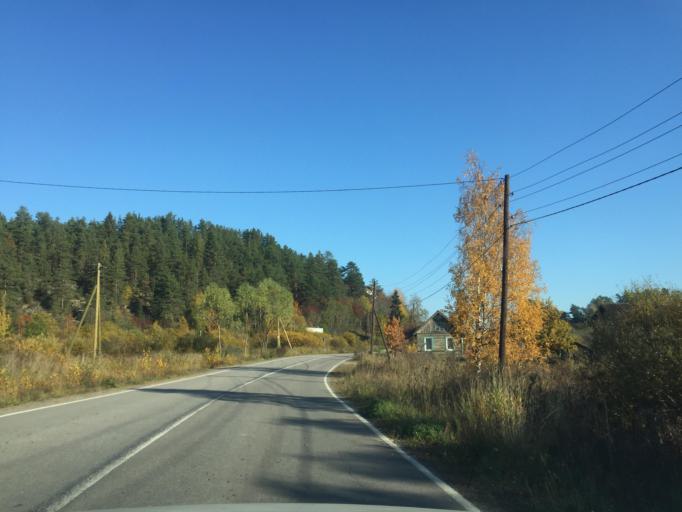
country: RU
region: Leningrad
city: Kuznechnoye
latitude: 61.3012
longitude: 29.9124
